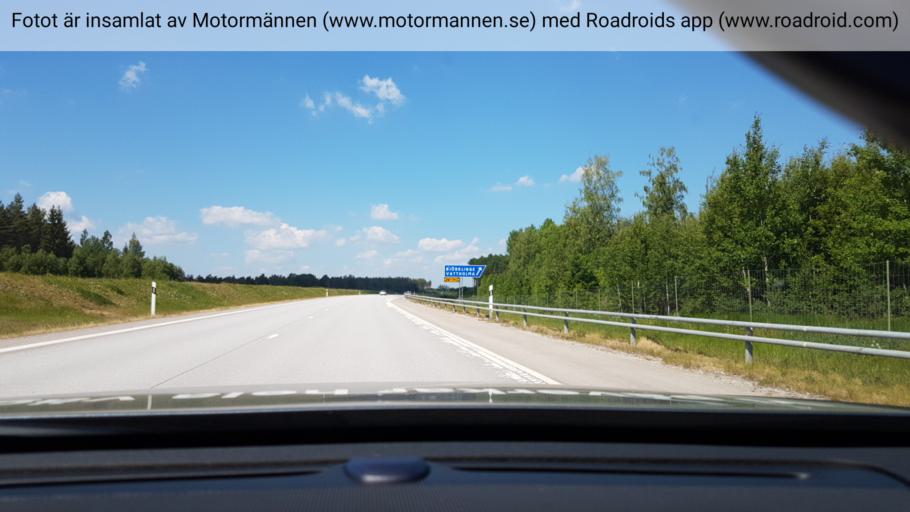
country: SE
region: Uppsala
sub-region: Osthammars Kommun
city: Bjorklinge
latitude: 60.0073
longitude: 17.6262
